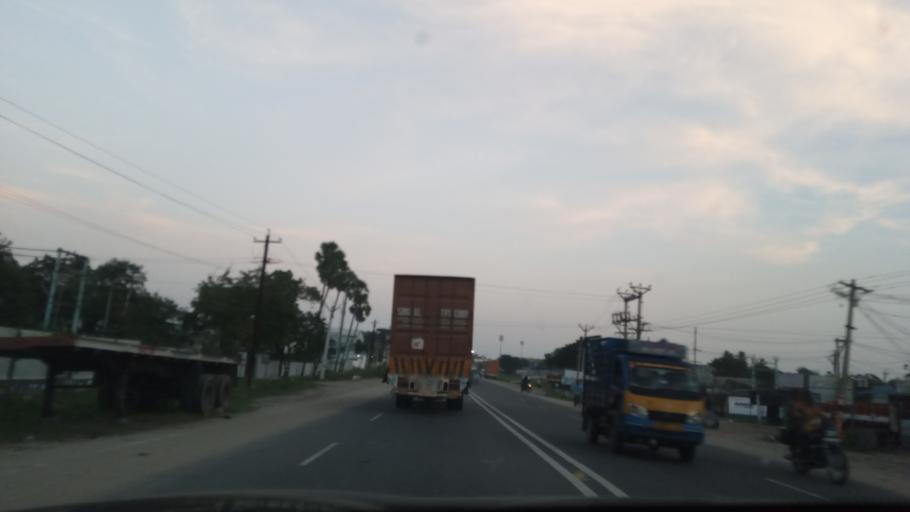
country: IN
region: Tamil Nadu
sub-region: Vellore
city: Walajapet
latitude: 12.9285
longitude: 79.3445
